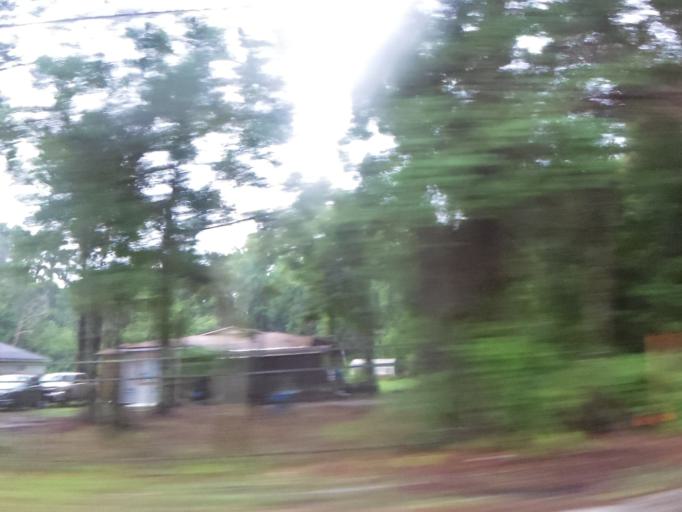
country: US
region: Florida
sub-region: Duval County
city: Jacksonville
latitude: 30.2791
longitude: -81.5679
